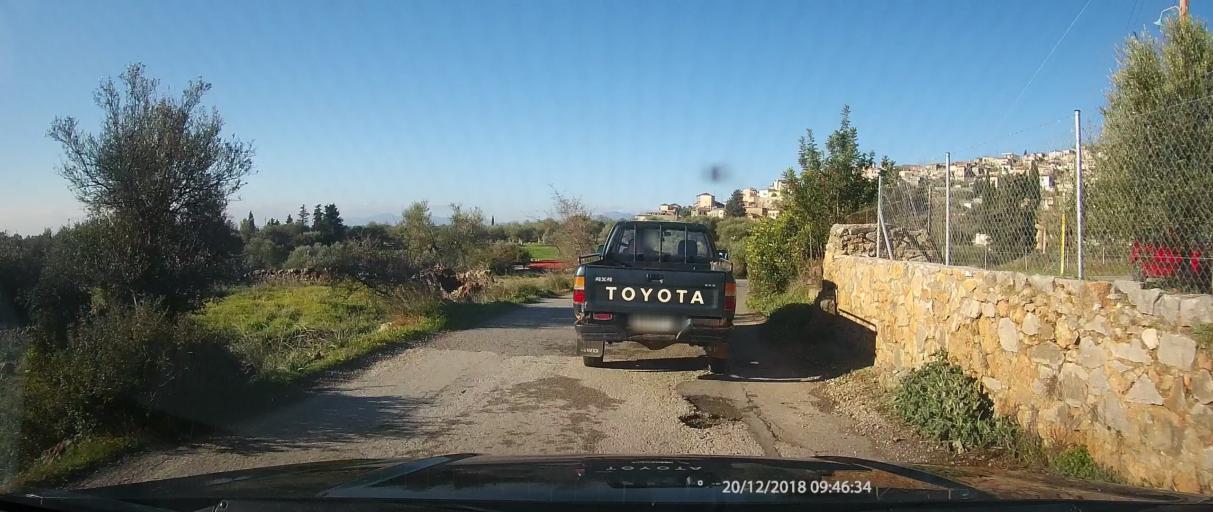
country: GR
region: Peloponnese
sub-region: Nomos Lakonias
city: Yerakion
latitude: 36.9920
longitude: 22.7133
